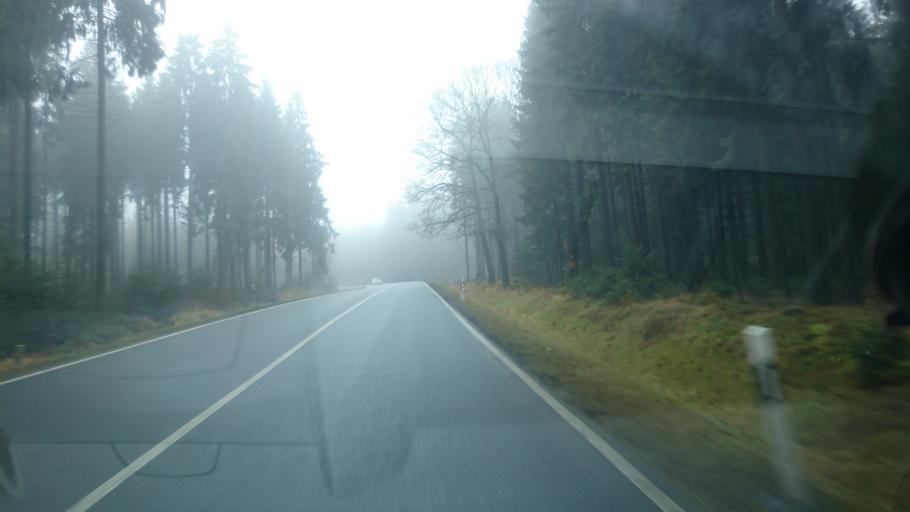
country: DE
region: Thuringia
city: Tanna
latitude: 50.4567
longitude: 11.8536
